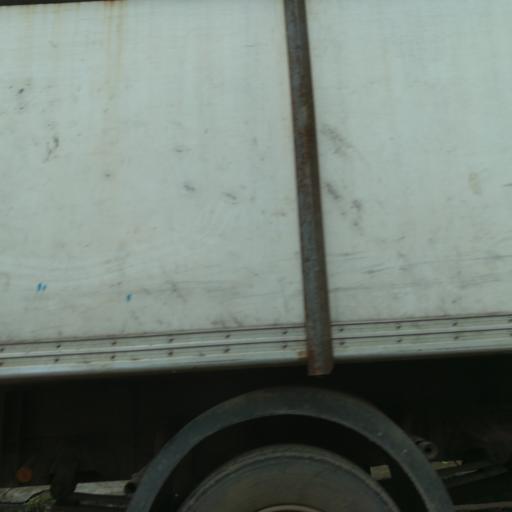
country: NG
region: Lagos
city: Agege
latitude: 6.5960
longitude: 3.2965
